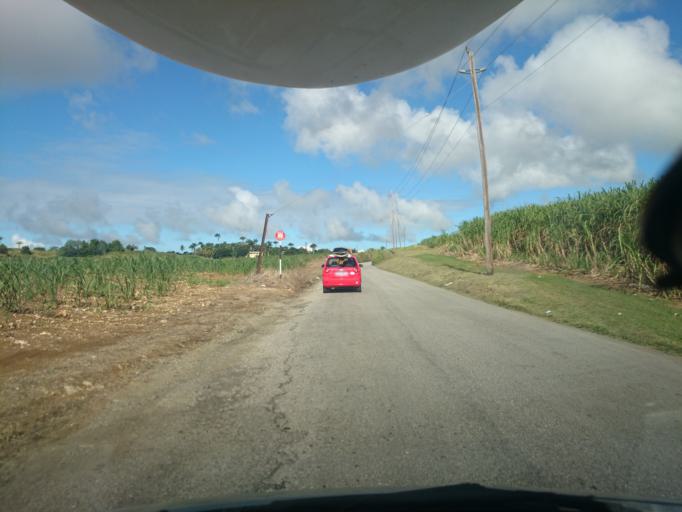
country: BB
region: Saint Thomas
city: Welchman Hall
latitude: 13.1642
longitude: -59.5554
